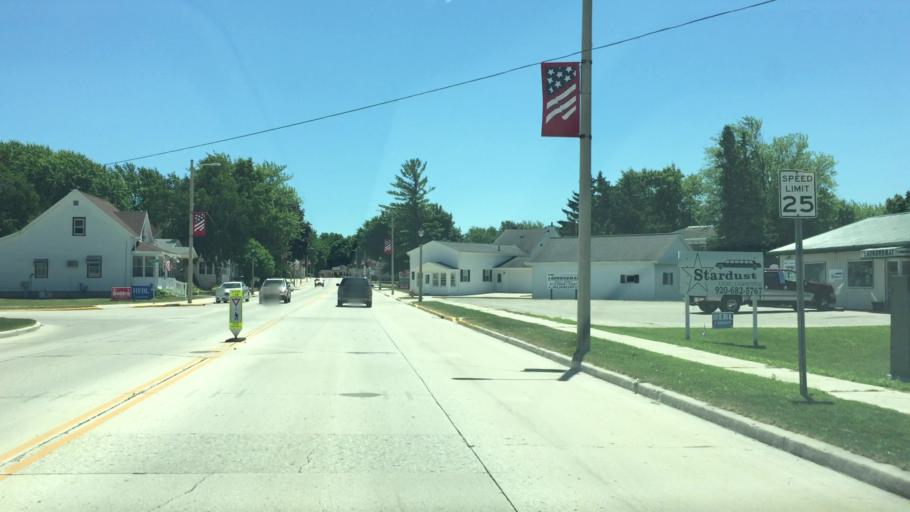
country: US
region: Wisconsin
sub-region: Calumet County
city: New Holstein
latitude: 43.9522
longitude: -88.1017
